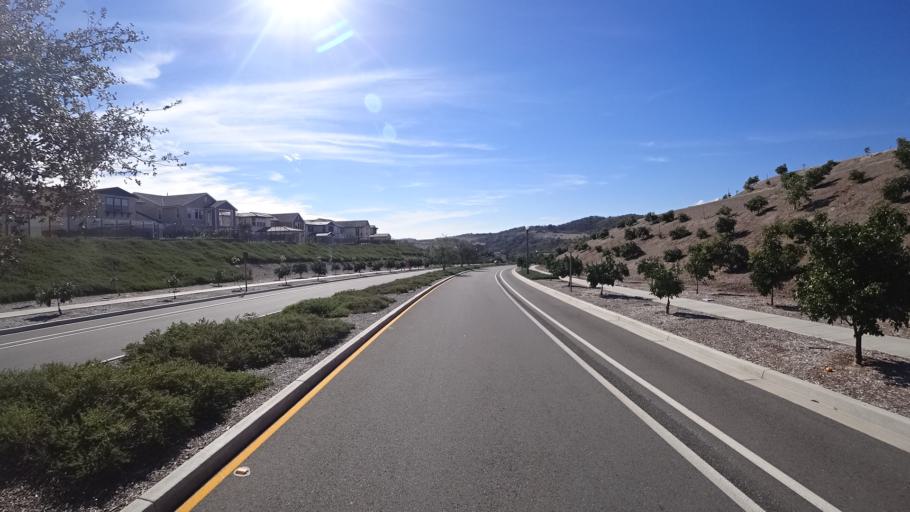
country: US
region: California
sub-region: Orange County
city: Ladera Ranch
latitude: 33.5424
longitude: -117.6039
